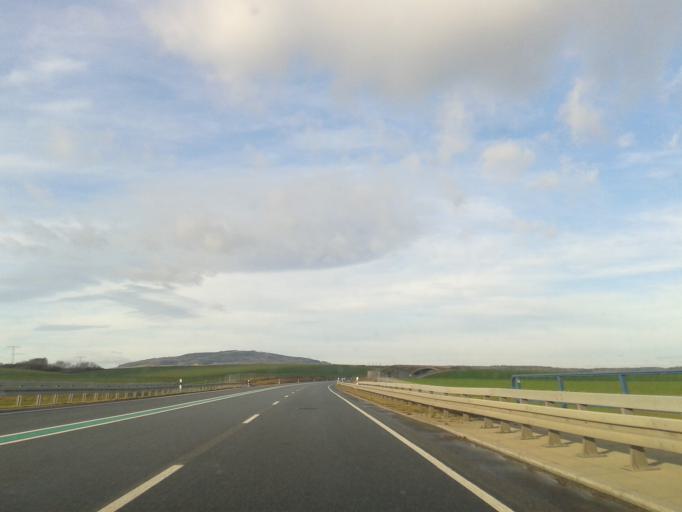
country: DE
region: Saxony
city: Herrnhut
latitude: 50.9729
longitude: 14.7366
